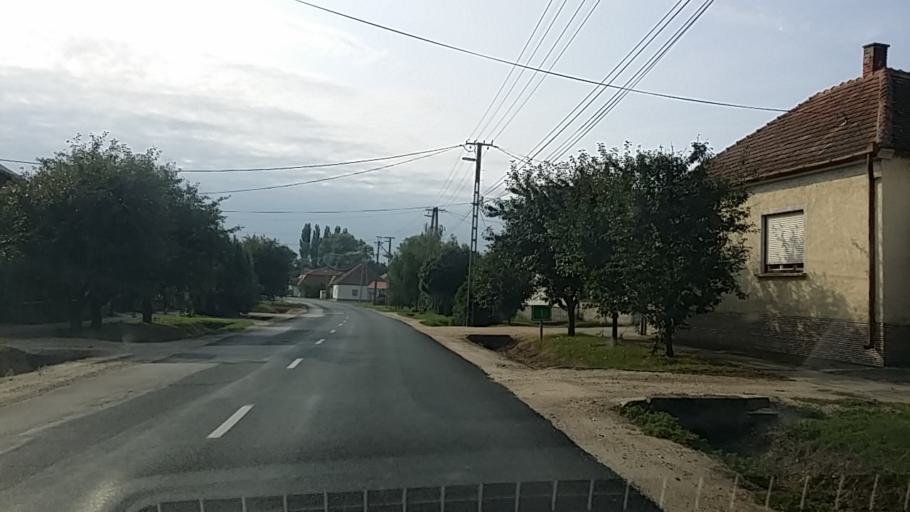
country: HU
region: Gyor-Moson-Sopron
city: Fertoszentmiklos
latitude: 47.6042
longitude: 16.9078
